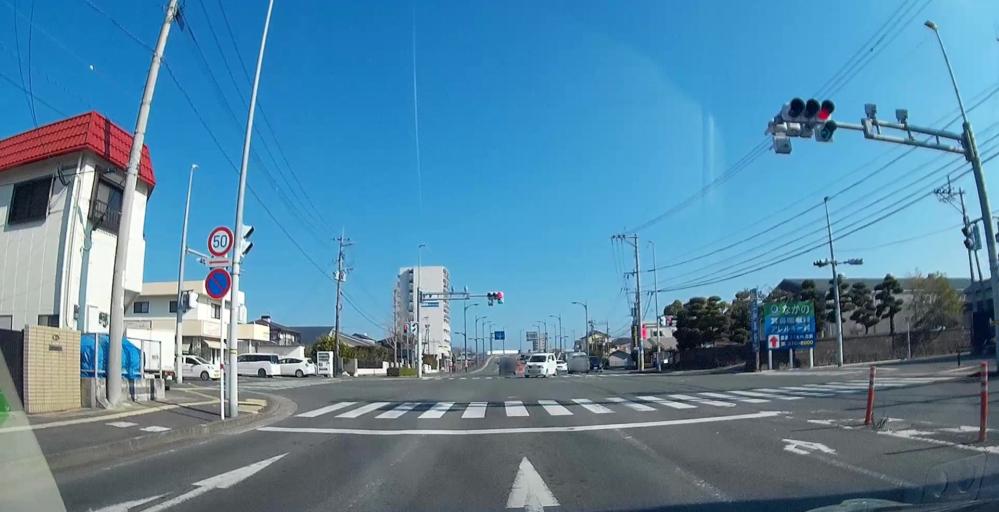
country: JP
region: Kumamoto
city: Kumamoto
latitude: 32.7723
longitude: 130.6873
